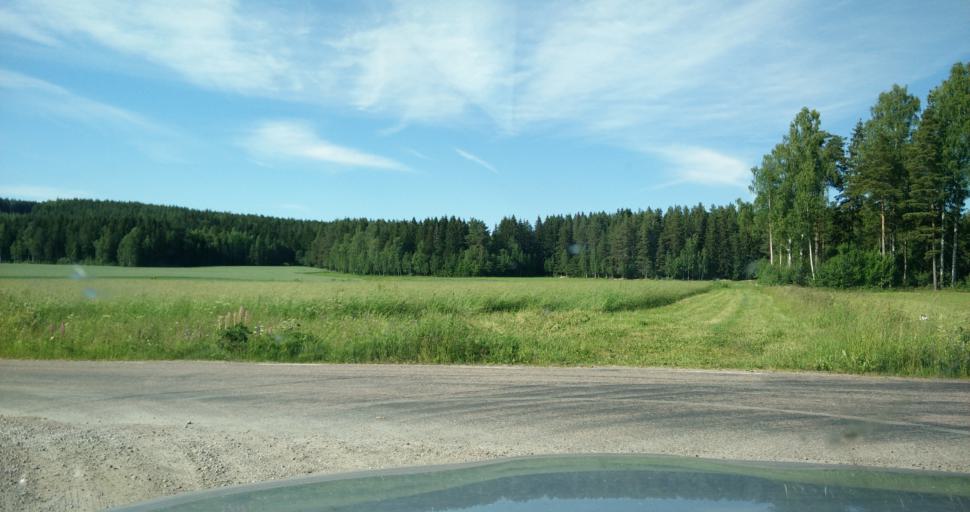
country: SE
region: Dalarna
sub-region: Hedemora Kommun
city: Langshyttan
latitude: 60.3926
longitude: 15.9592
